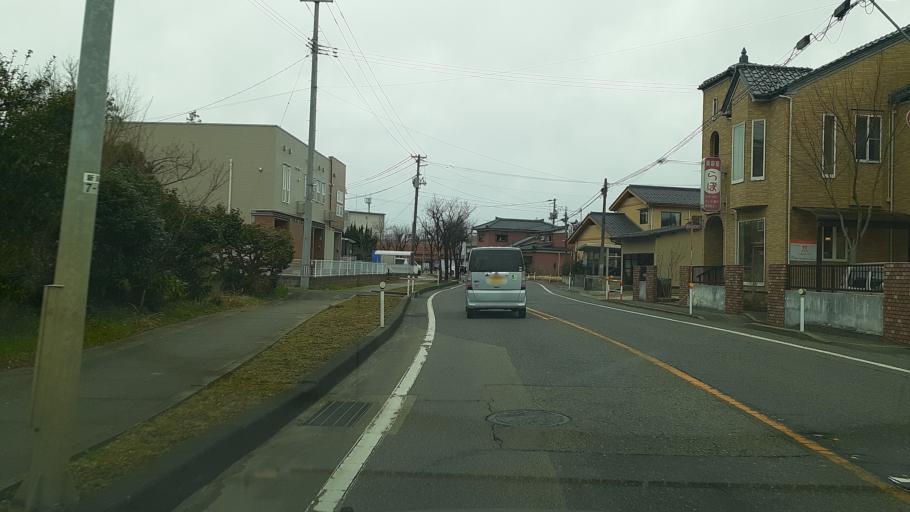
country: JP
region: Niigata
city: Niitsu-honcho
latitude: 37.7935
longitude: 139.1360
